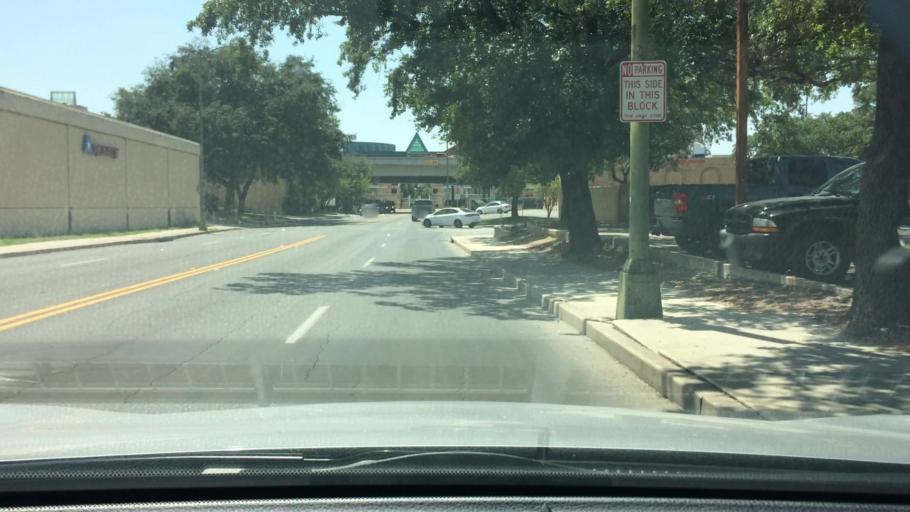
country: US
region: Texas
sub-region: Bexar County
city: San Antonio
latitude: 29.4235
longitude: -98.4999
